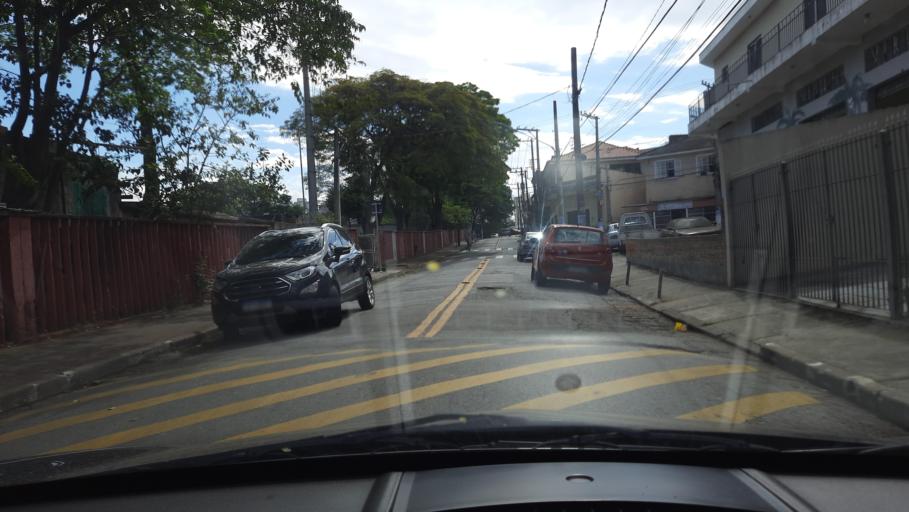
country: BR
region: Sao Paulo
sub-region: Osasco
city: Osasco
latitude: -23.4876
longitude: -46.7119
